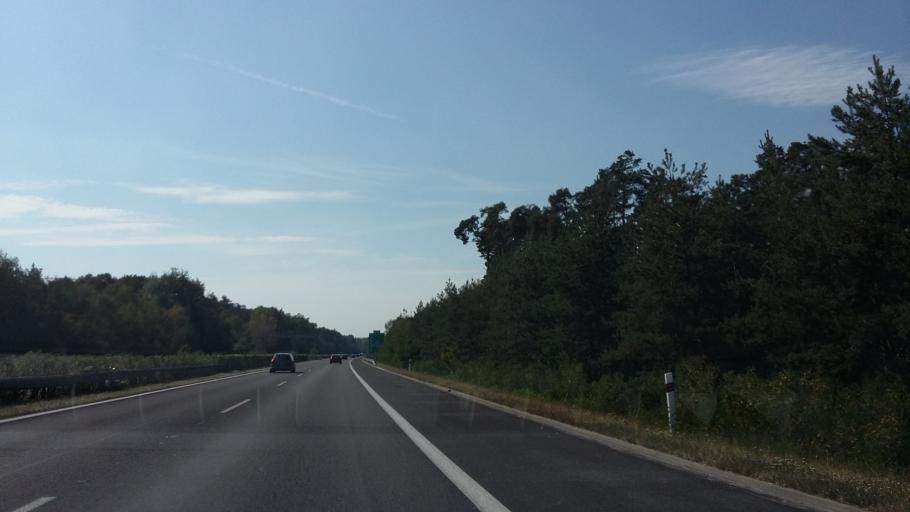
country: CZ
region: Central Bohemia
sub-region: Okres Nymburk
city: Podebrady
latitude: 50.1176
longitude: 15.1417
